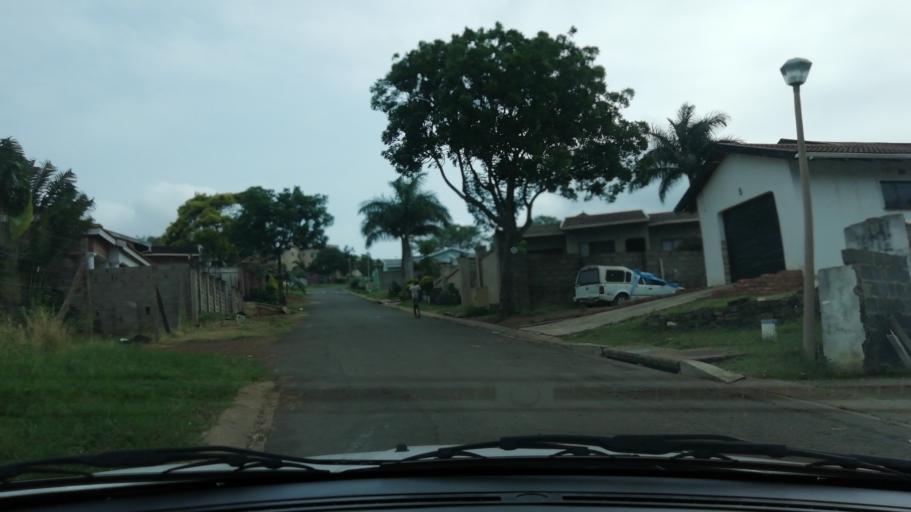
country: ZA
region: KwaZulu-Natal
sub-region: uThungulu District Municipality
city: Empangeni
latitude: -28.7374
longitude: 31.8790
